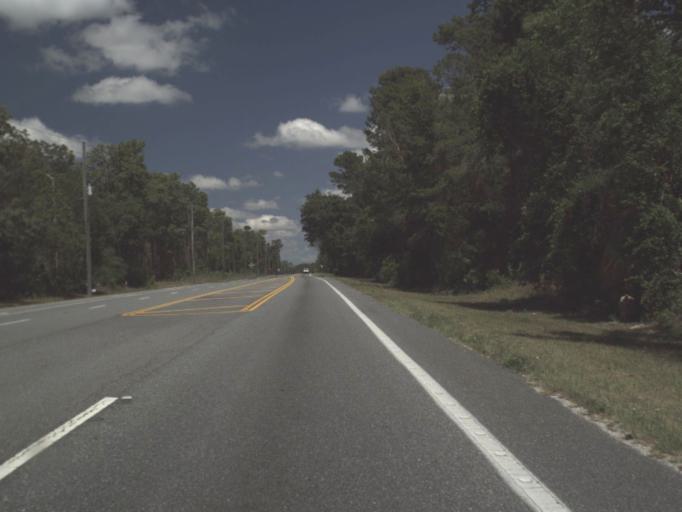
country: US
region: Florida
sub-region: Marion County
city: Silver Springs Shores
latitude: 29.2031
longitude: -81.9371
